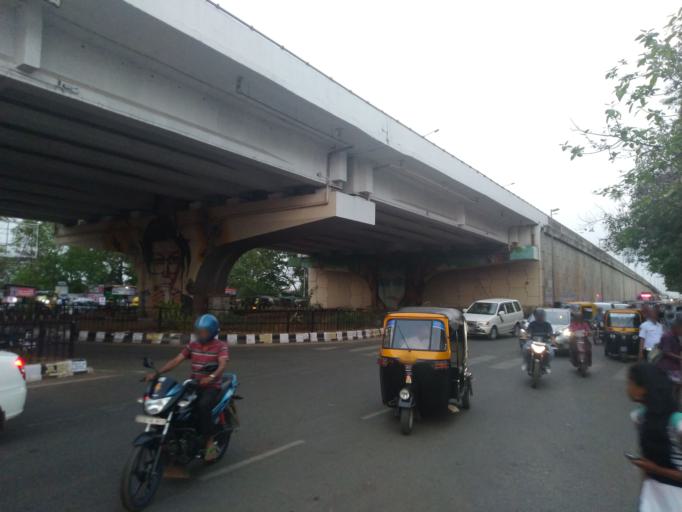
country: IN
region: Odisha
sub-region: Khordha
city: Bhubaneshwar
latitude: 20.2960
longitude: 85.8423
